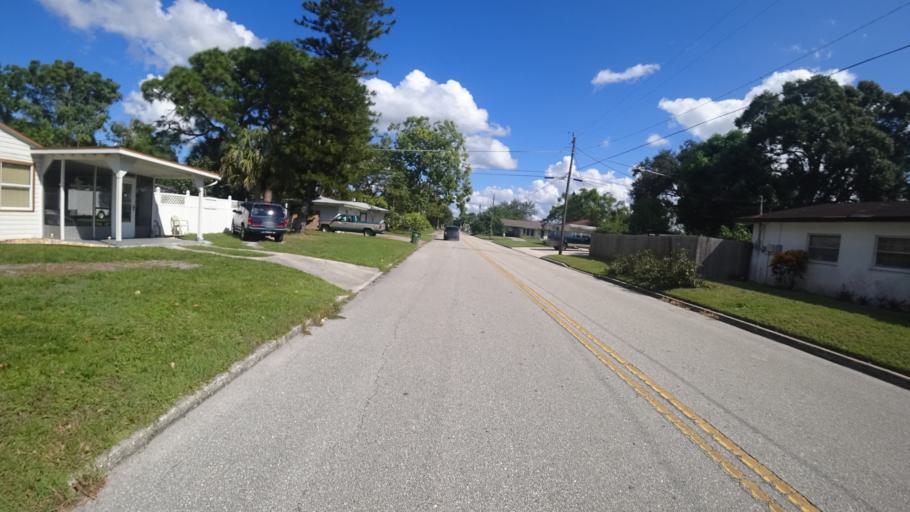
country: US
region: Florida
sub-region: Manatee County
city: South Bradenton
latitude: 27.4810
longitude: -82.5809
